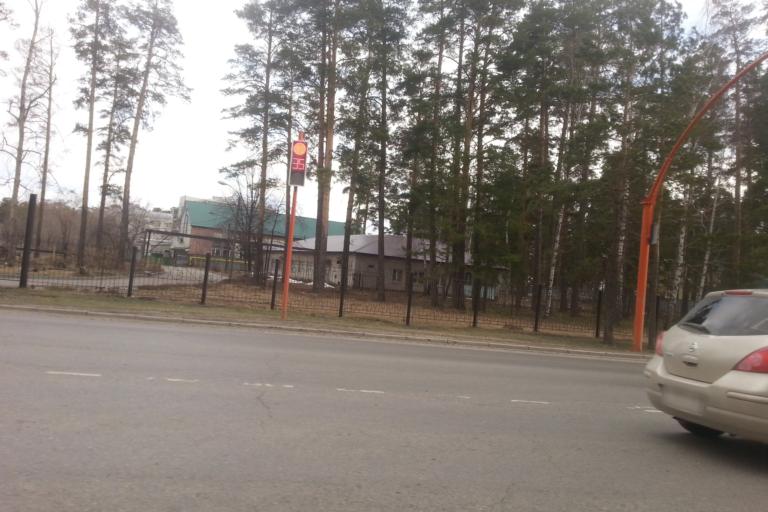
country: RU
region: Altai Krai
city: Zaton
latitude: 53.2819
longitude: 83.7495
